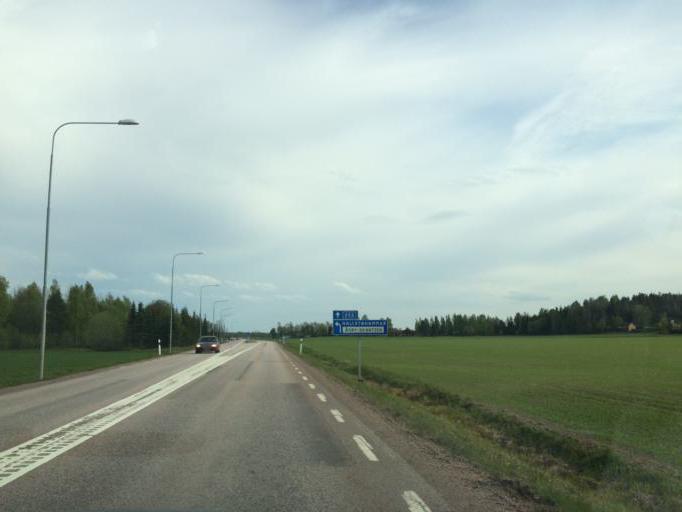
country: SE
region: Vaestmanland
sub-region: Hallstahammars Kommun
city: Hallstahammar
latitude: 59.6062
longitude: 16.2023
